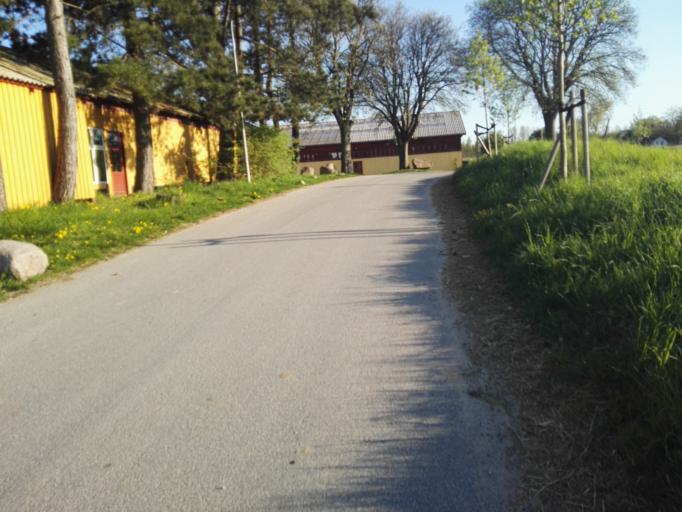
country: DK
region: Capital Region
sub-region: Ballerup Kommune
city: Malov
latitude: 55.7358
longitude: 12.3373
